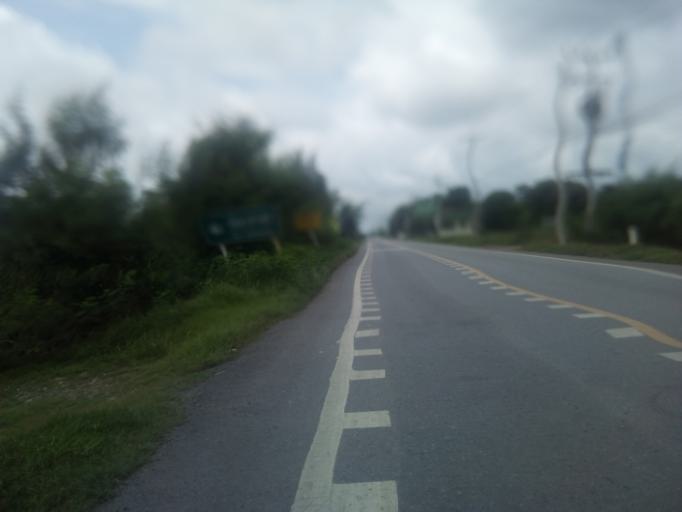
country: TH
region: Pathum Thani
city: Ban Lam Luk Ka
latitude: 14.0119
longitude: 100.8229
